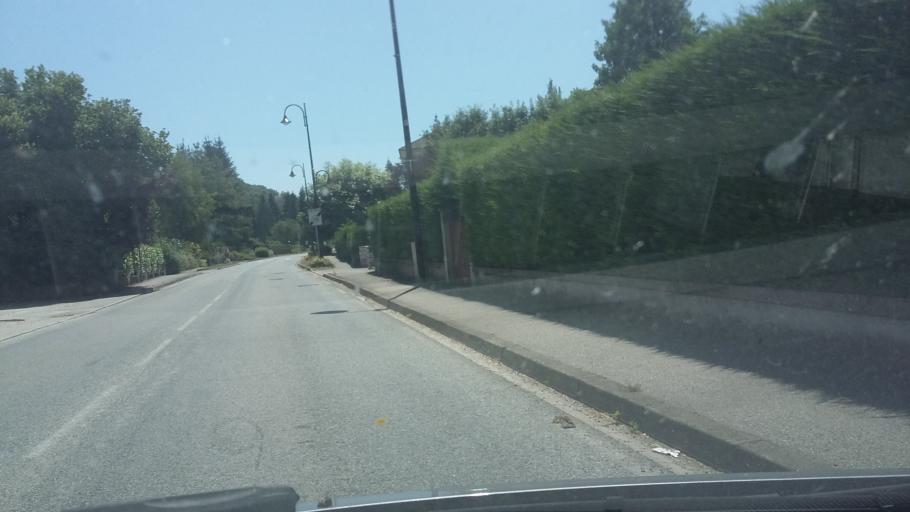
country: FR
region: Rhone-Alpes
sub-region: Departement de l'Ain
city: Belley
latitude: 45.8021
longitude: 5.6818
